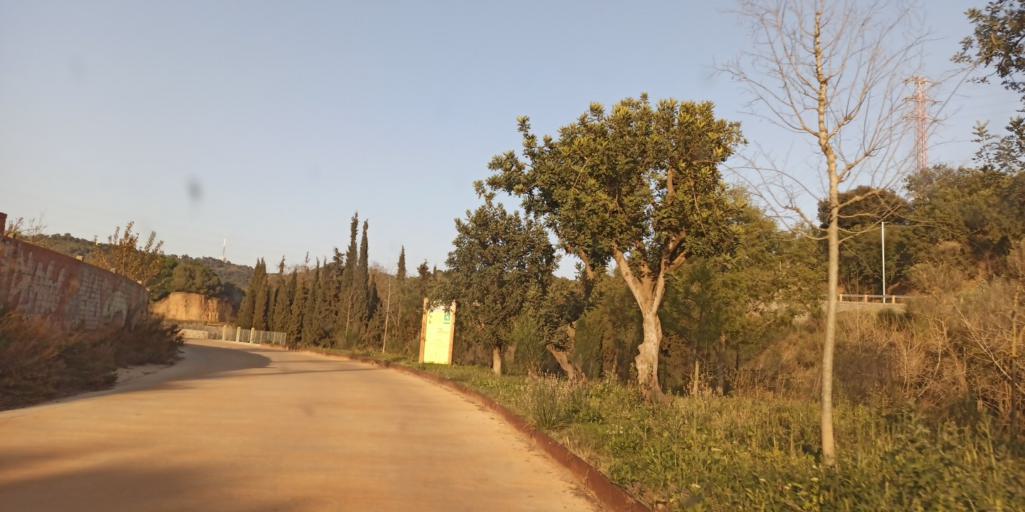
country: ES
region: Catalonia
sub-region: Provincia de Barcelona
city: Sant Just Desvern
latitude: 41.3941
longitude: 2.0794
